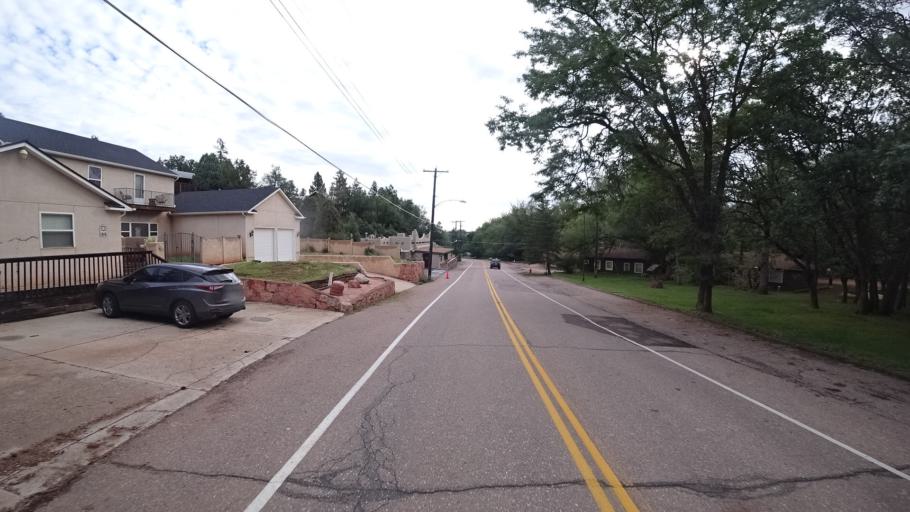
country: US
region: Colorado
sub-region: El Paso County
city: Manitou Springs
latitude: 38.8522
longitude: -104.8972
